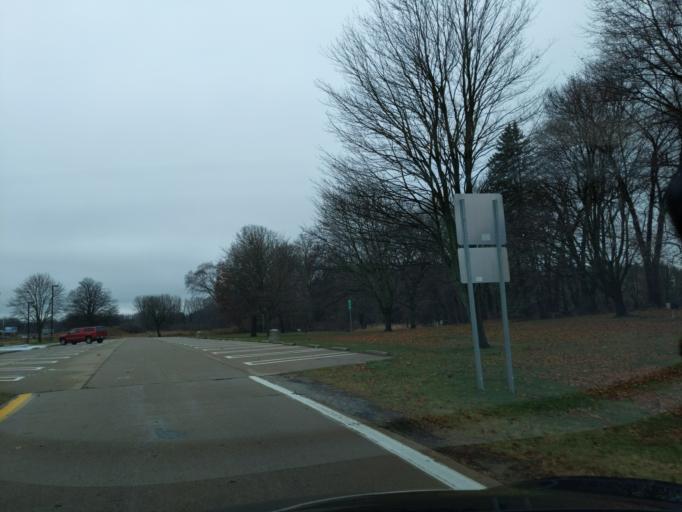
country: US
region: Michigan
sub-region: Ingham County
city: Leslie
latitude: 42.3654
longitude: -84.4302
